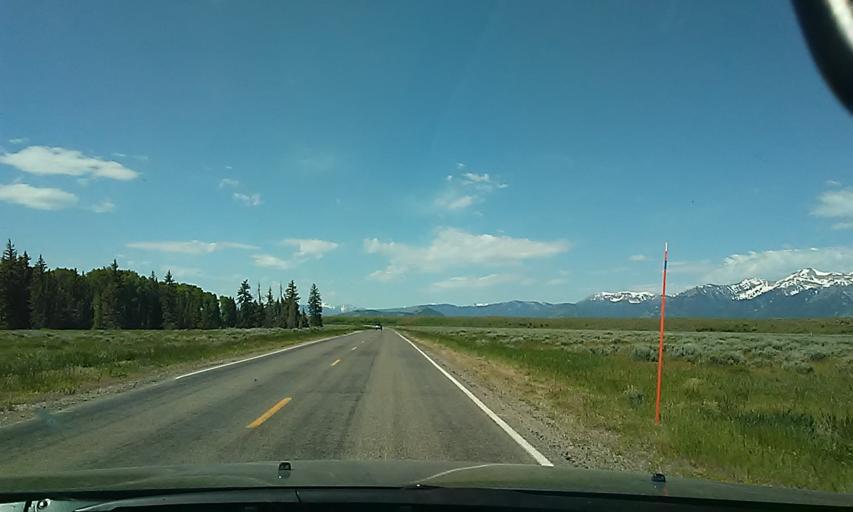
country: US
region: Wyoming
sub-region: Teton County
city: Jackson
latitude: 43.6077
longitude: -110.6884
